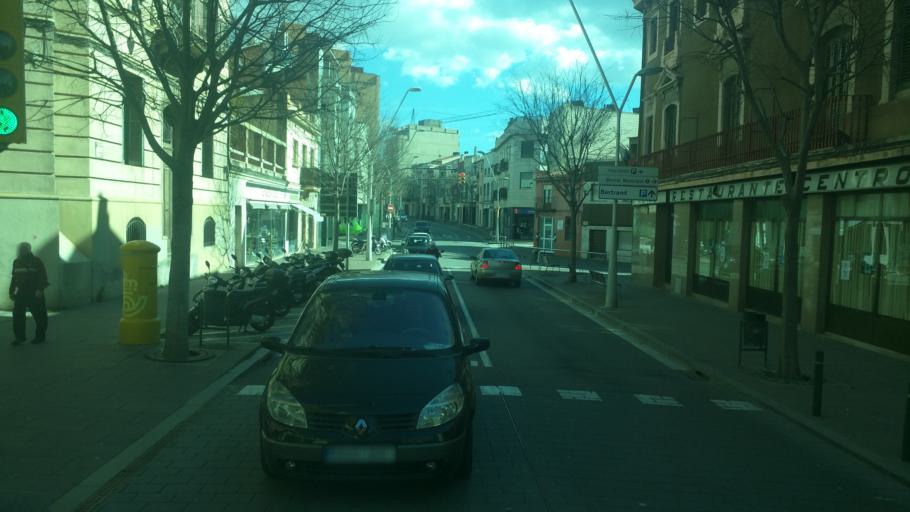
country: ES
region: Catalonia
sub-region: Provincia de Barcelona
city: Sant Feliu de Llobregat
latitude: 41.3809
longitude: 2.0445
